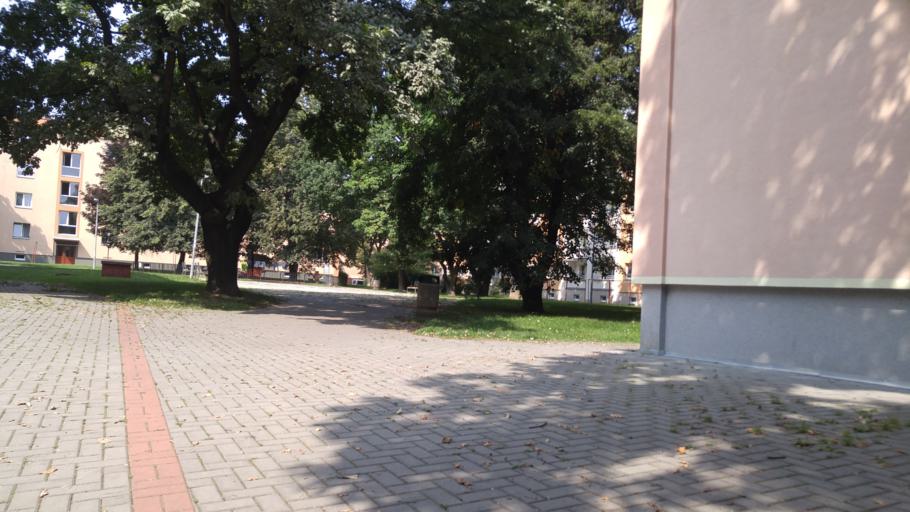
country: CZ
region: Central Bohemia
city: Horomerice
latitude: 50.0904
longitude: 14.3476
